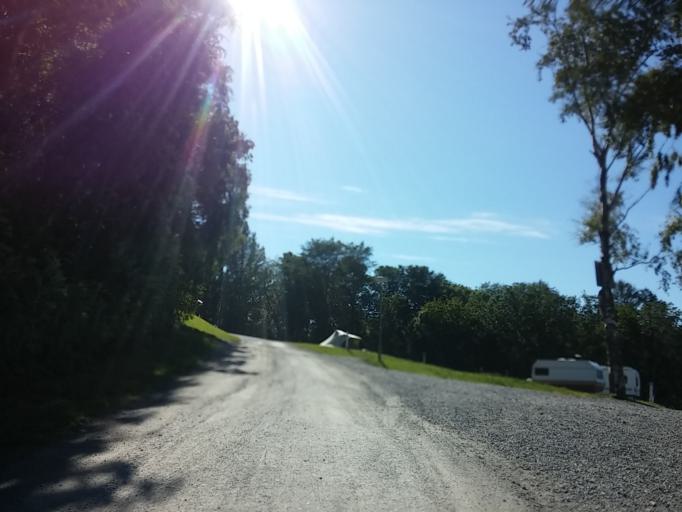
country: NO
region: Sor-Trondelag
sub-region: Malvik
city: Malvik
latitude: 63.4346
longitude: 10.7084
